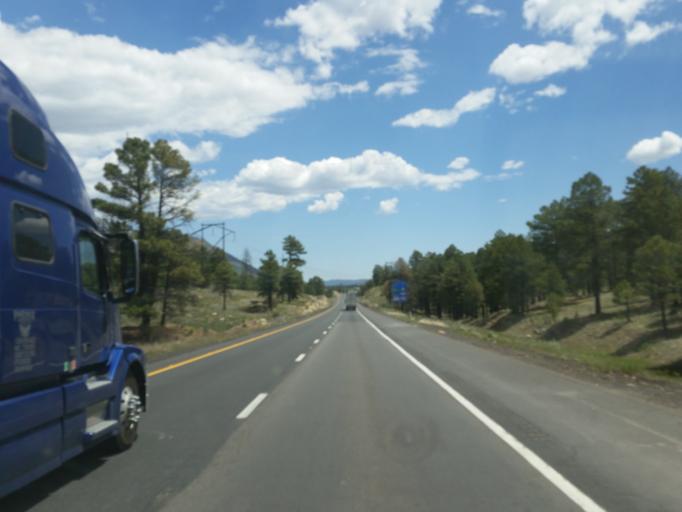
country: US
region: Arizona
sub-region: Coconino County
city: Flagstaff
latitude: 35.1766
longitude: -111.6419
